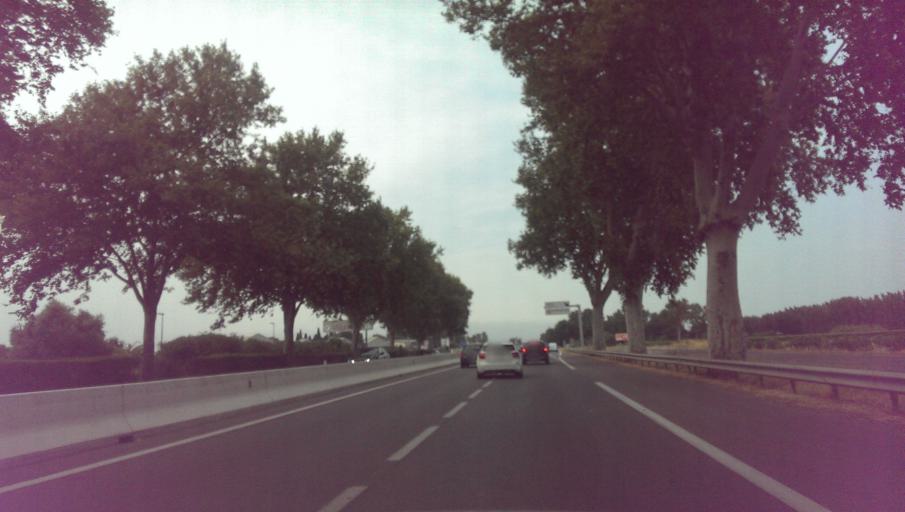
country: FR
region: Languedoc-Roussillon
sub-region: Departement des Pyrenees-Orientales
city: Rivesaltes
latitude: 42.7660
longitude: 2.8994
